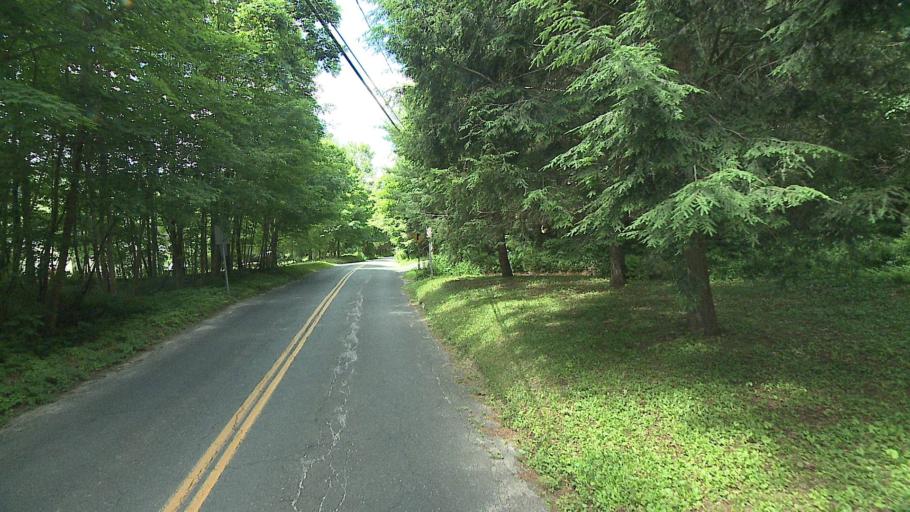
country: US
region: Connecticut
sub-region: Litchfield County
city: Litchfield
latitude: 41.8418
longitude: -73.3153
